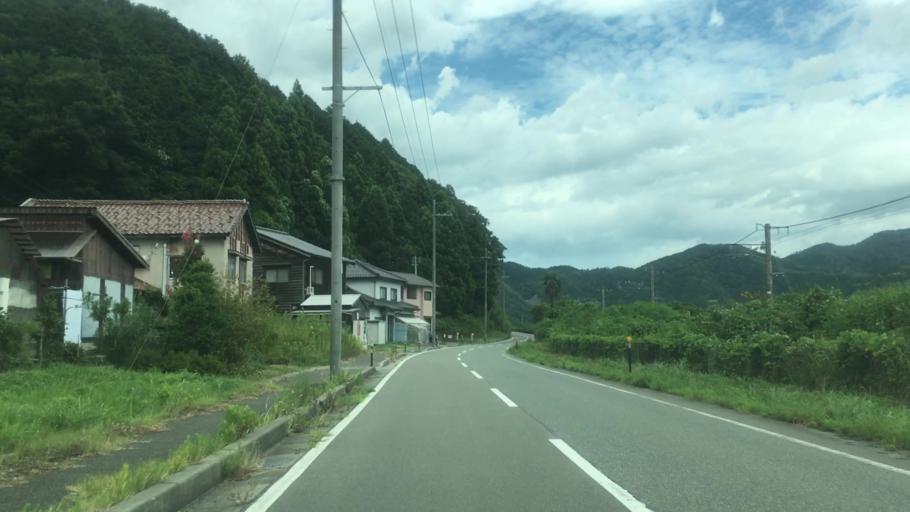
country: JP
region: Hyogo
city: Toyooka
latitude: 35.5707
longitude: 134.8044
